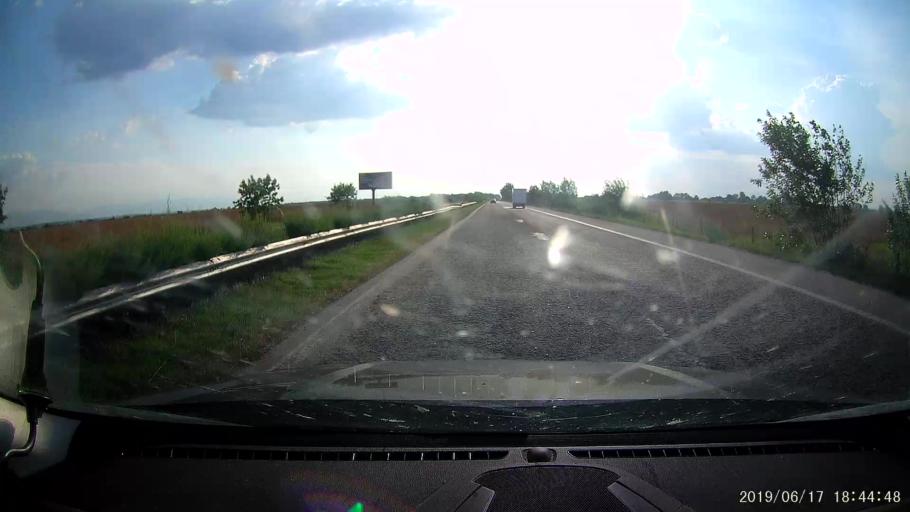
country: BG
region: Stara Zagora
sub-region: Obshtina Chirpan
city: Chirpan
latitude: 42.1934
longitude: 25.1701
